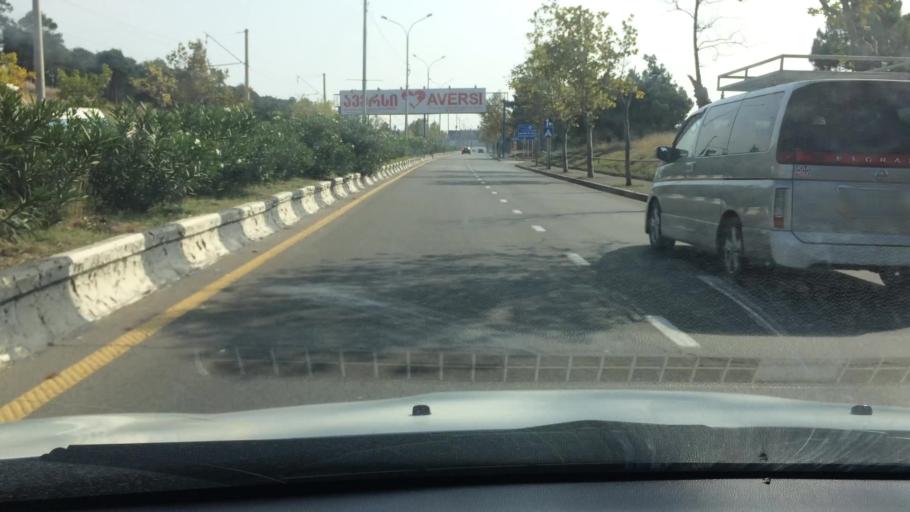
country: GE
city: Didi Lilo
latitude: 41.6778
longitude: 44.9595
